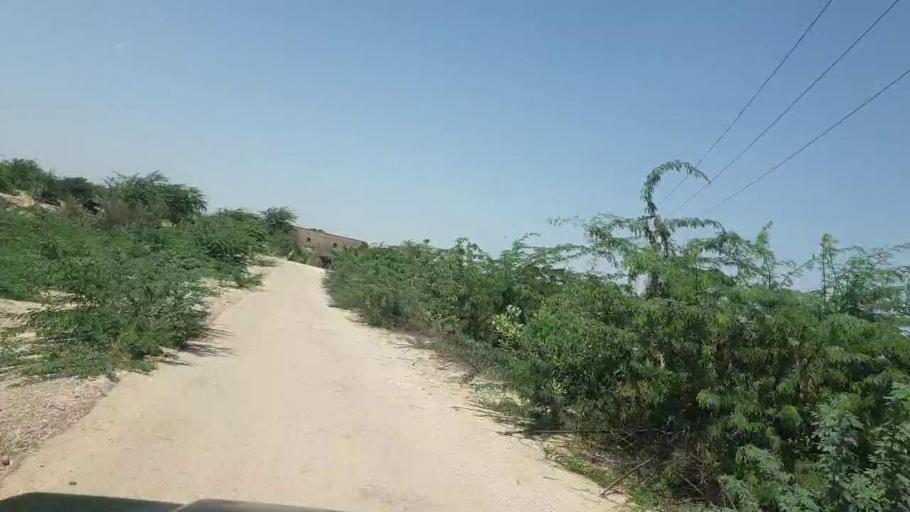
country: PK
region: Sindh
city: Chor
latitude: 25.4106
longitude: 70.3062
